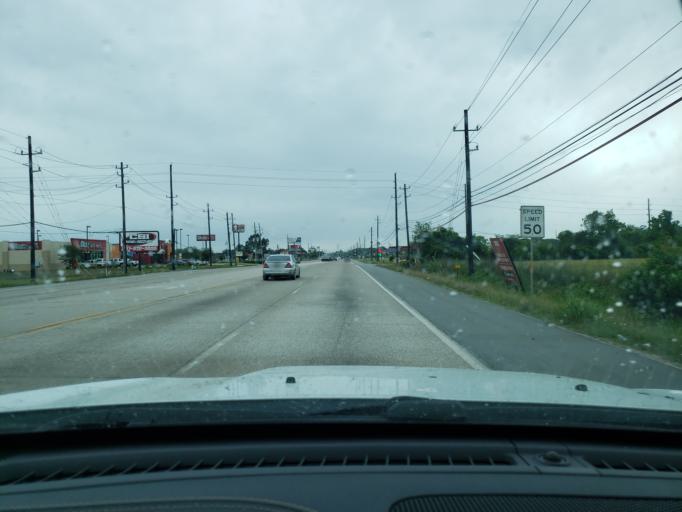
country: US
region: Texas
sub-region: Chambers County
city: Mont Belvieu
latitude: 29.8144
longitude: -94.9013
